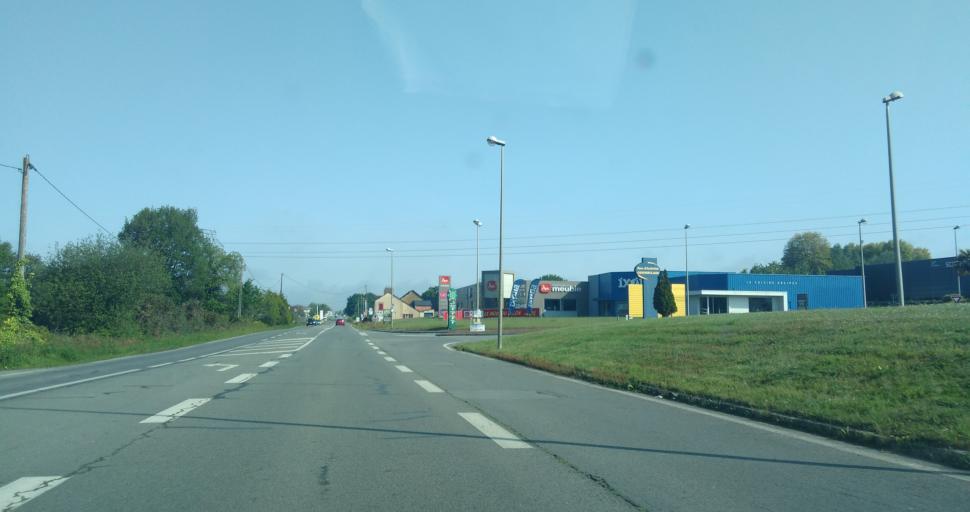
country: FR
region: Brittany
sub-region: Departement d'Ille-et-Vilaine
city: La Chapelle-des-Fougeretz
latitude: 48.1857
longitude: -1.7255
